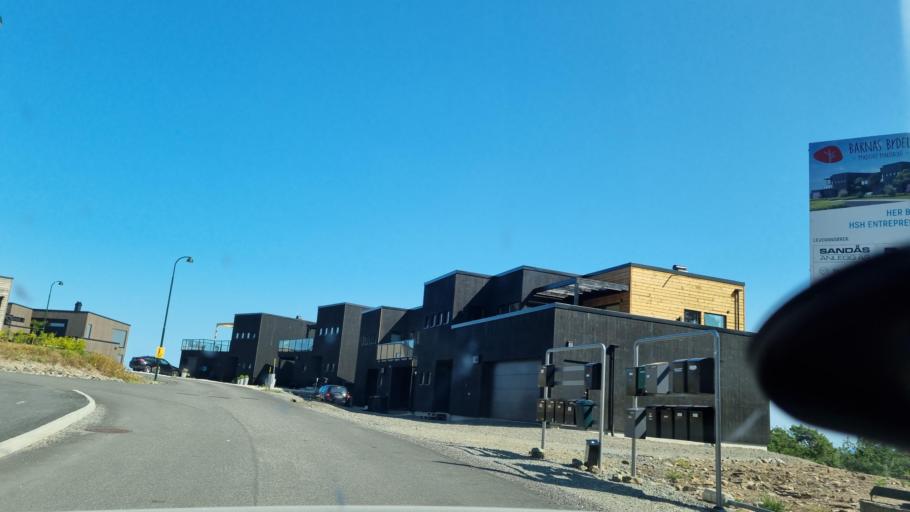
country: NO
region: Aust-Agder
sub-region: Arendal
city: Arendal
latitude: 58.4576
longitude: 8.8136
